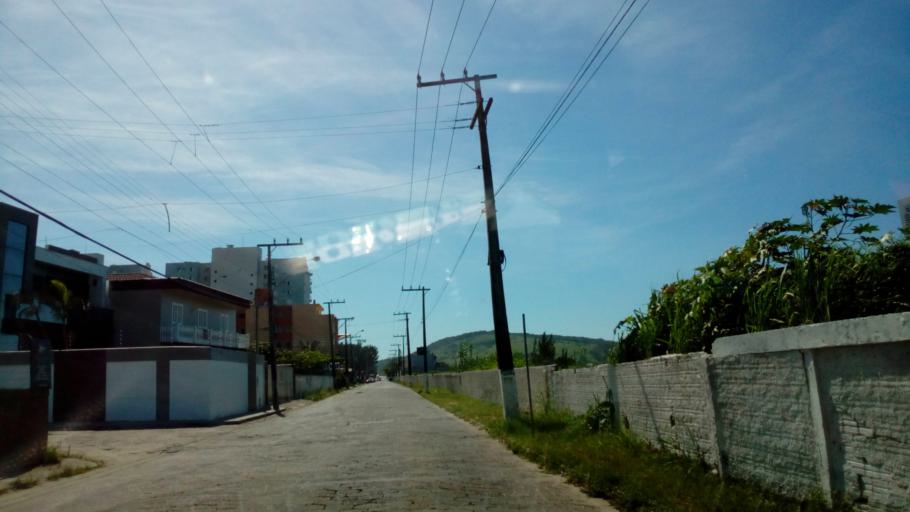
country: BR
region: Santa Catarina
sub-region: Laguna
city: Laguna
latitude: -28.4938
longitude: -48.7709
